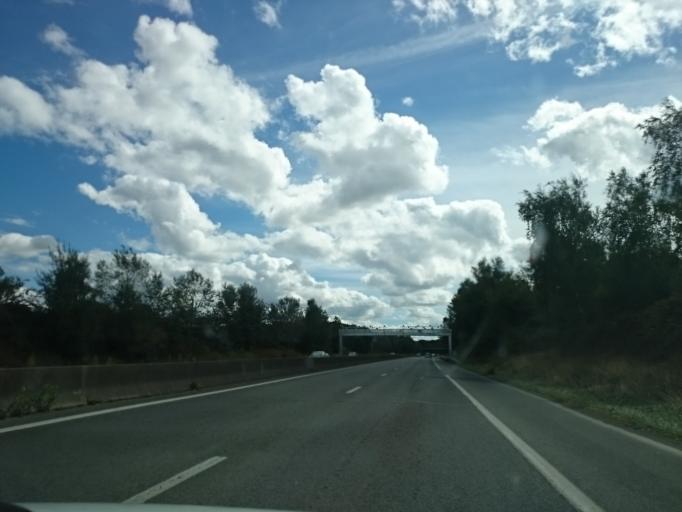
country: FR
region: Pays de la Loire
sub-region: Departement de la Loire-Atlantique
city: Basse-Goulaine
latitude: 47.2046
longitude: -1.4839
